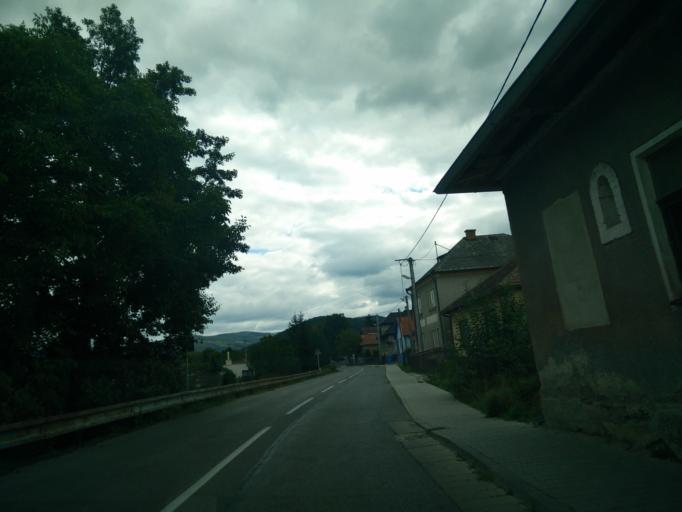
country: SK
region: Nitriansky
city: Partizanske
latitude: 48.6081
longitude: 18.4913
